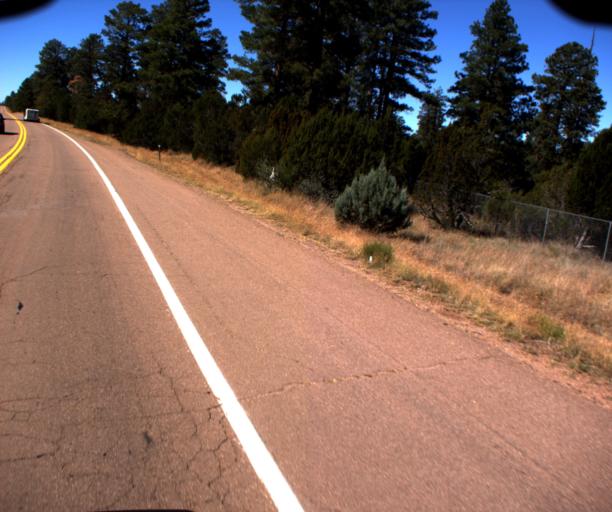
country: US
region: Arizona
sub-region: Navajo County
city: Heber-Overgaard
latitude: 34.4293
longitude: -110.5506
